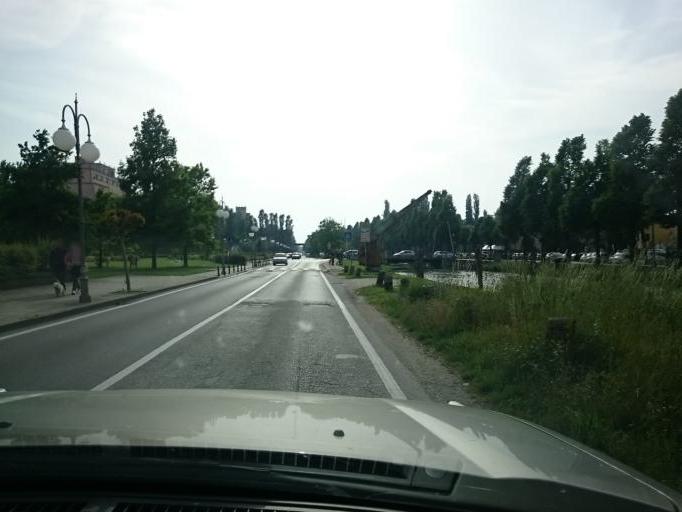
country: IT
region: Veneto
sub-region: Provincia di Venezia
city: Mira Taglio
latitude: 45.4340
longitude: 12.1335
